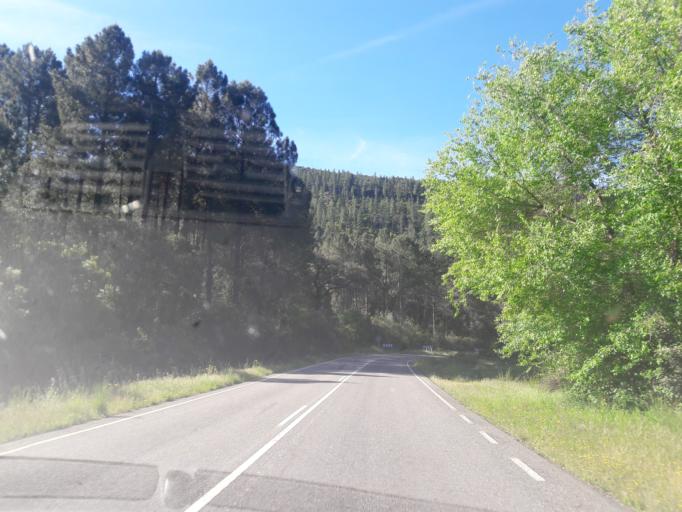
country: ES
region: Castille and Leon
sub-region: Provincia de Salamanca
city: Sotoserrano
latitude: 40.4073
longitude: -6.0524
